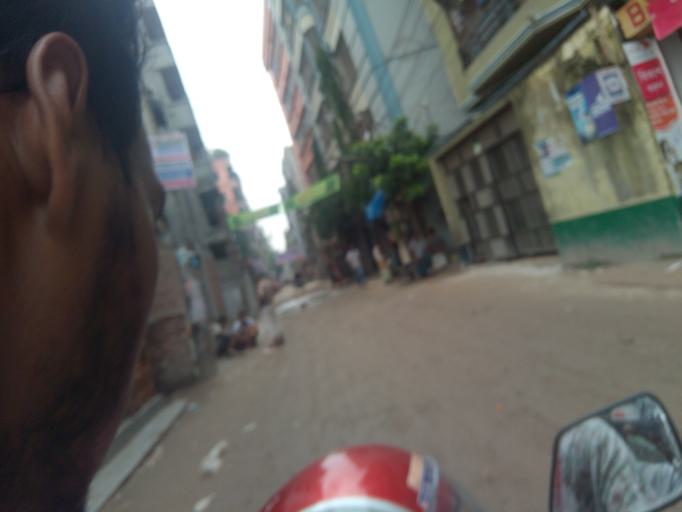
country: BD
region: Dhaka
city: Paltan
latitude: 23.7586
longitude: 90.4285
